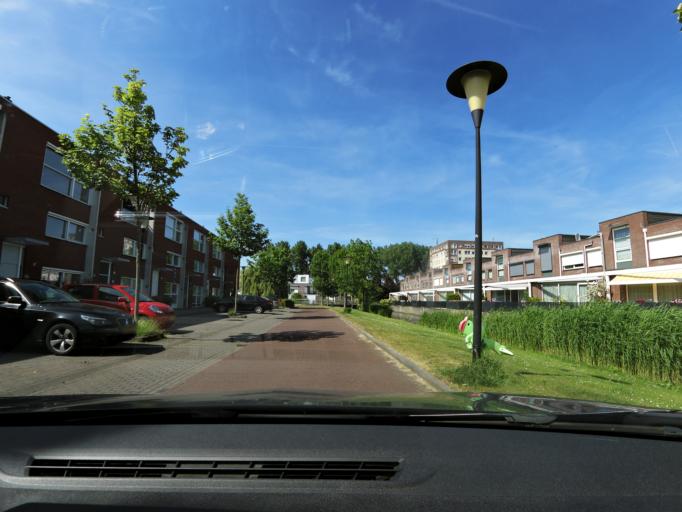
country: NL
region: South Holland
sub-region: Gemeente Barendrecht
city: Barendrecht
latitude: 51.8463
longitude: 4.5057
